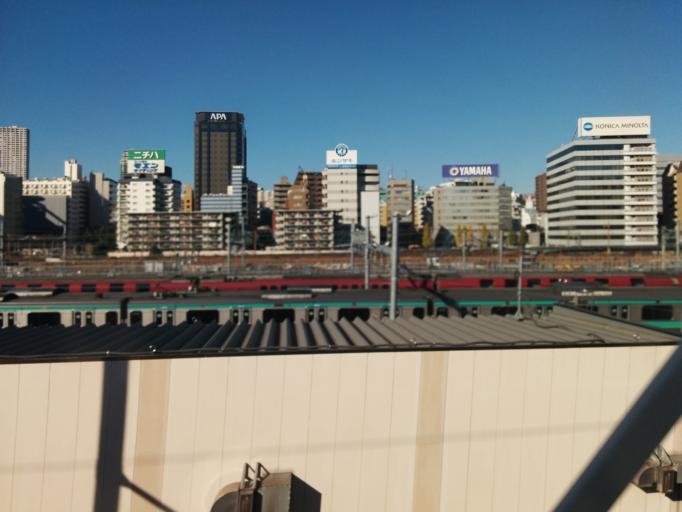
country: JP
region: Tokyo
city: Tokyo
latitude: 35.6374
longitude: 139.7429
